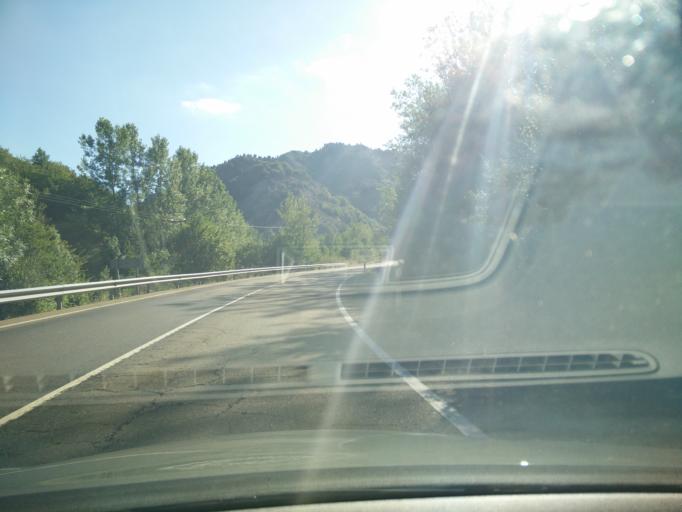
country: ES
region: Castille and Leon
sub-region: Provincia de Leon
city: Cremenes
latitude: 42.9322
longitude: -5.1089
